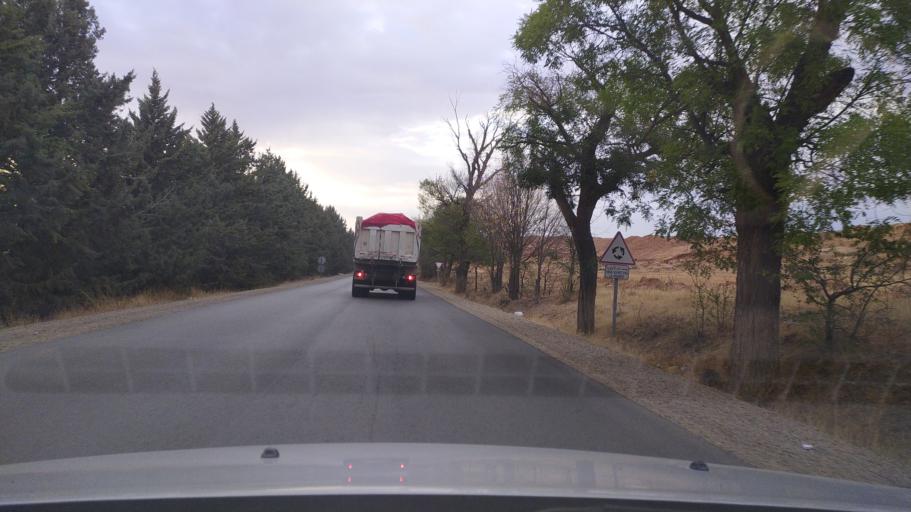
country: DZ
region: Tiaret
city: Frenda
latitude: 35.0499
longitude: 1.0767
